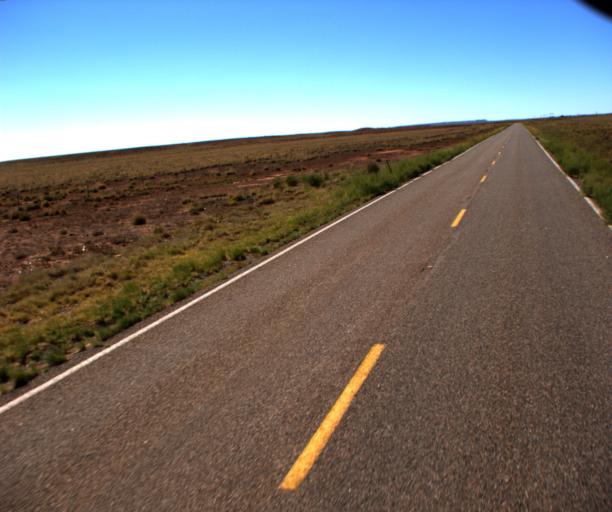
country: US
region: Arizona
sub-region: Coconino County
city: LeChee
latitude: 35.1682
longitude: -110.9155
